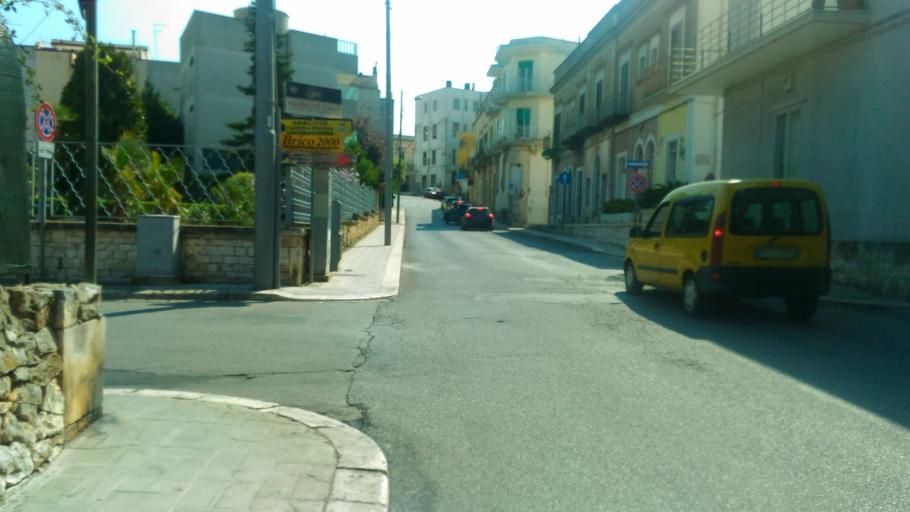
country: IT
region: Apulia
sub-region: Provincia di Bari
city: Locorotondo
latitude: 40.7549
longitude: 17.3250
